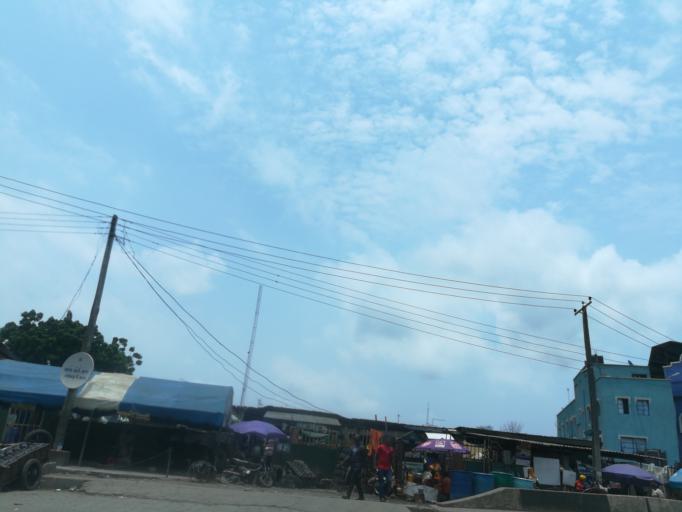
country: NG
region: Lagos
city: Lagos
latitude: 6.4556
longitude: 3.4054
